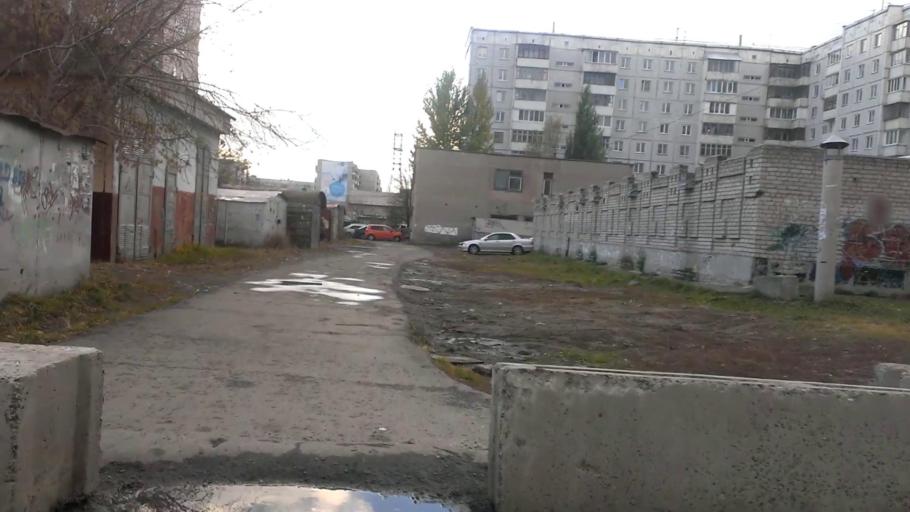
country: RU
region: Altai Krai
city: Novosilikatnyy
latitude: 53.3573
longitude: 83.6760
